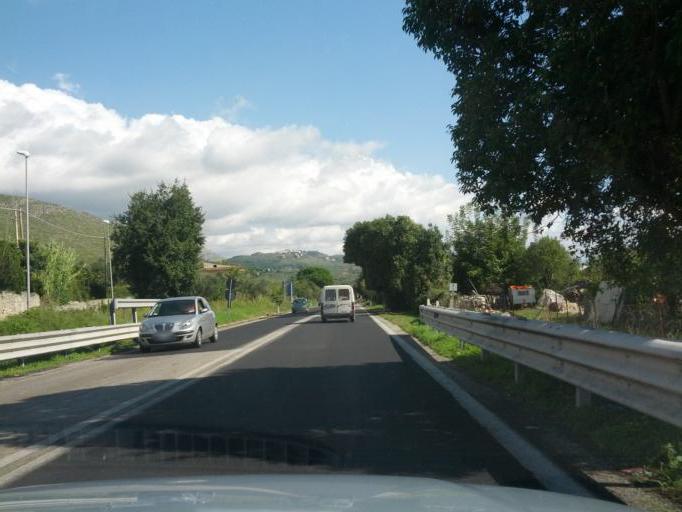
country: IT
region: Latium
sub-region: Provincia di Latina
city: Formia
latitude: 41.2666
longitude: 13.6334
